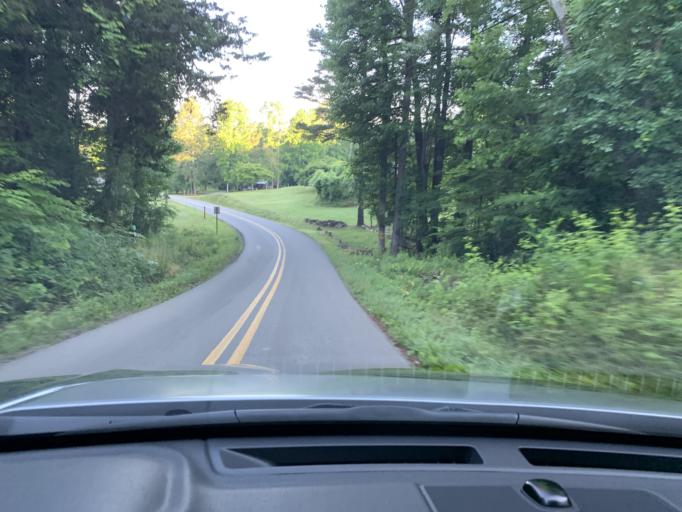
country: US
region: Georgia
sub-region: Bartow County
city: Rydal
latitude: 34.2494
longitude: -84.6788
